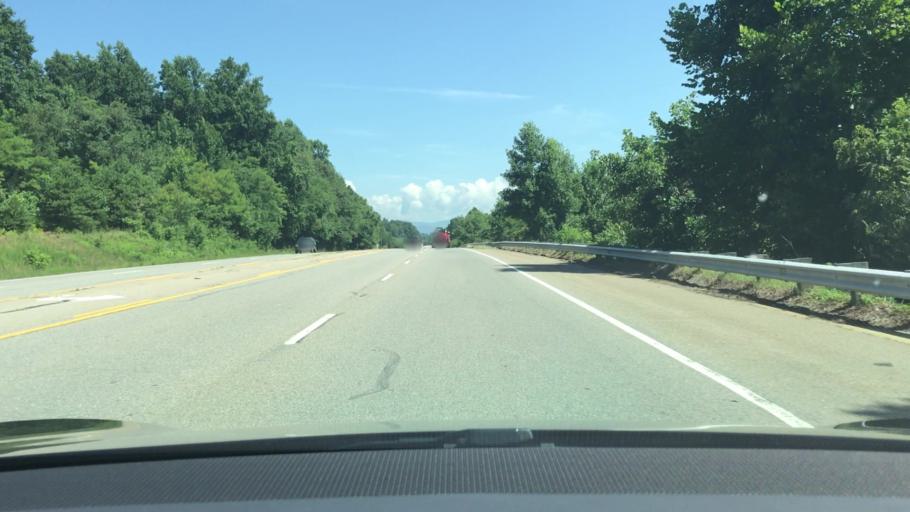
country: US
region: North Carolina
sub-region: Macon County
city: Franklin
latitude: 35.0783
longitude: -83.3849
